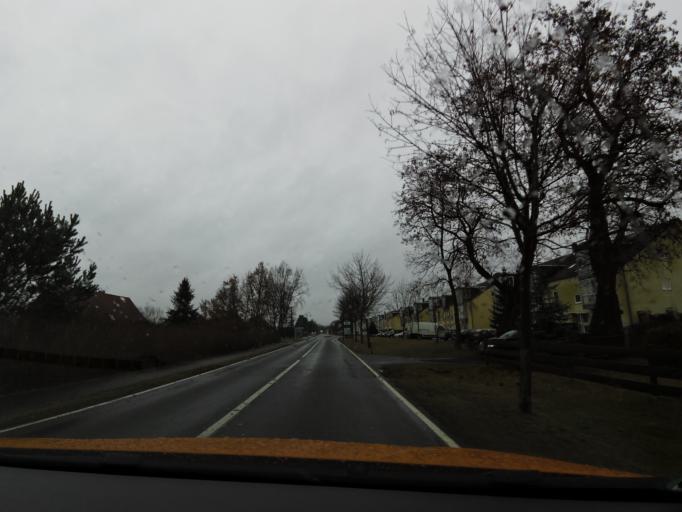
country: DE
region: Brandenburg
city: Zossen
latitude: 52.2019
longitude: 13.4319
